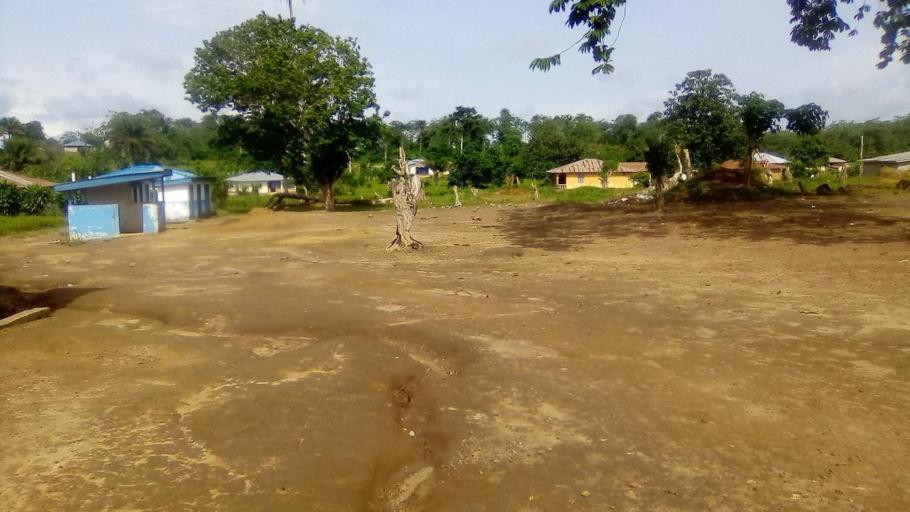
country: SL
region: Southern Province
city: Pujehun
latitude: 7.3675
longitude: -11.7266
